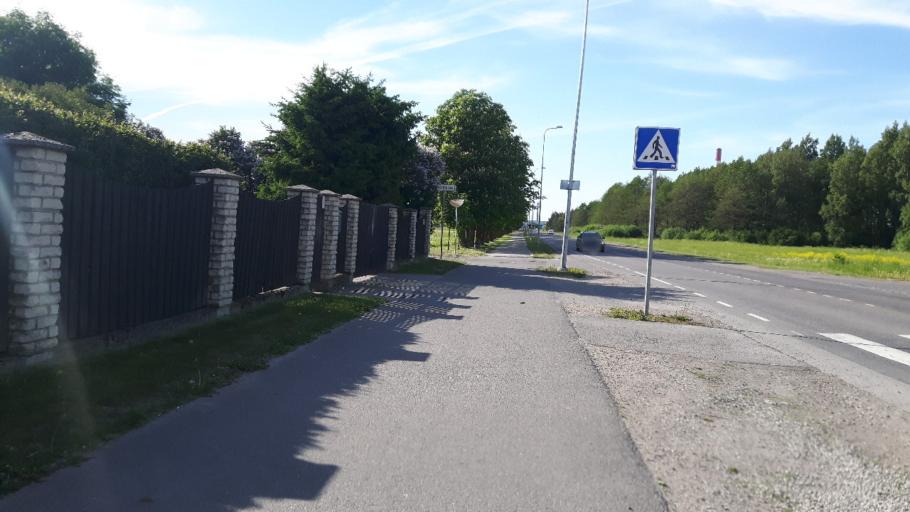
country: EE
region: Harju
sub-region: Joelaehtme vald
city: Loo
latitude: 59.4375
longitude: 24.9393
